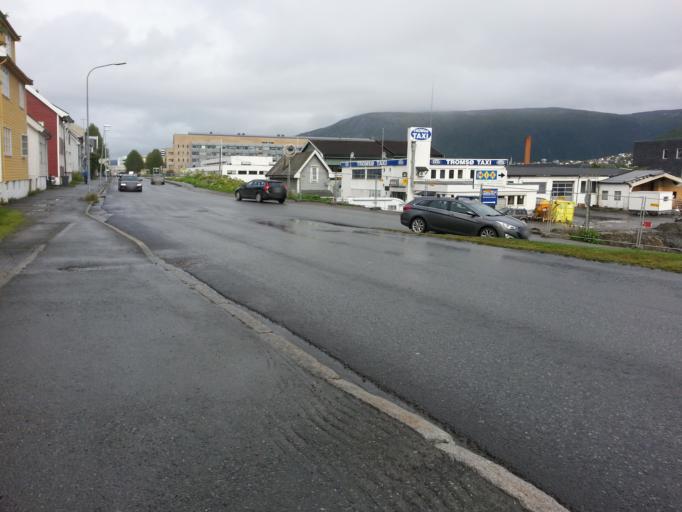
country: NO
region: Troms
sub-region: Tromso
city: Tromso
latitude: 69.6423
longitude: 18.9414
